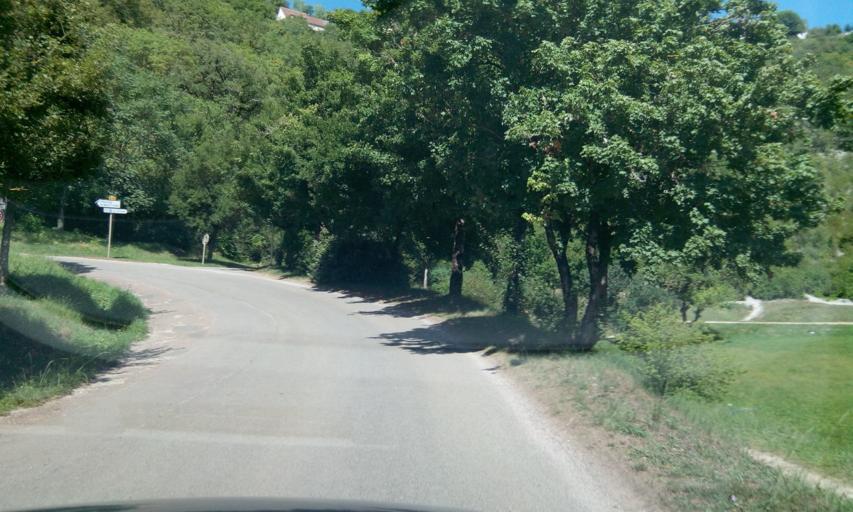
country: FR
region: Midi-Pyrenees
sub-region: Departement du Lot
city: Gramat
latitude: 44.8021
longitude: 1.6226
